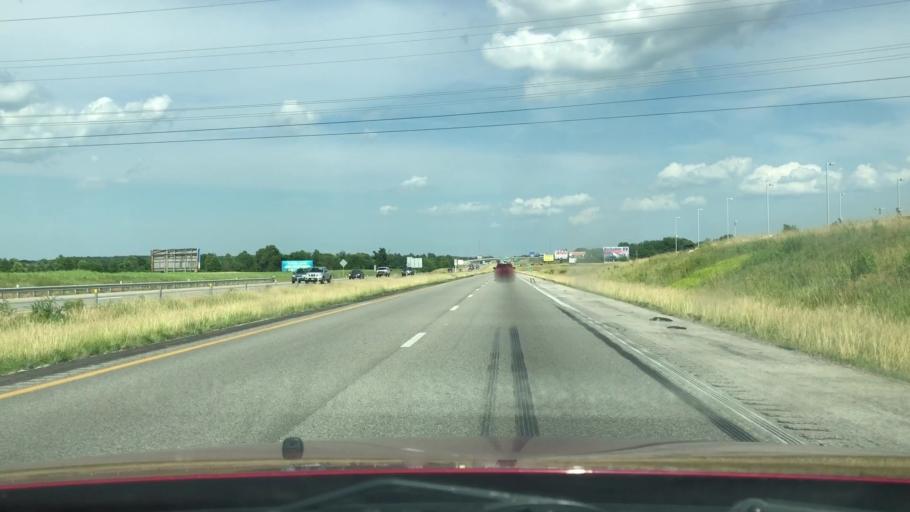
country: US
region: Missouri
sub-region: Greene County
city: Springfield
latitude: 37.2502
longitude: -93.2433
